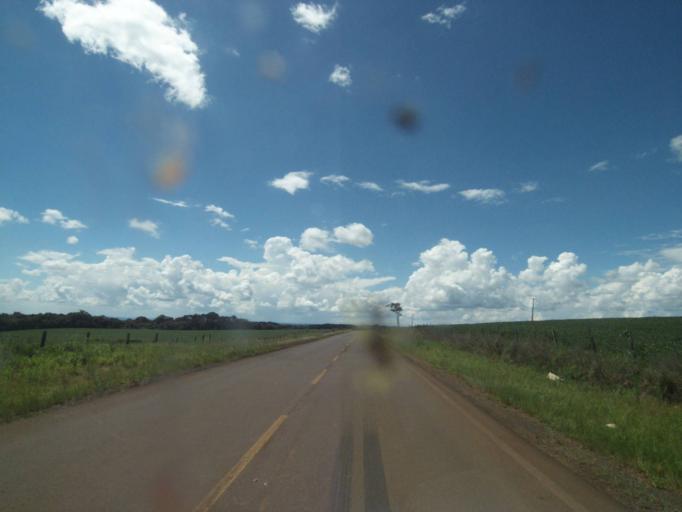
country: BR
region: Parana
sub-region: Pinhao
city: Pinhao
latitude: -25.8024
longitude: -52.0738
